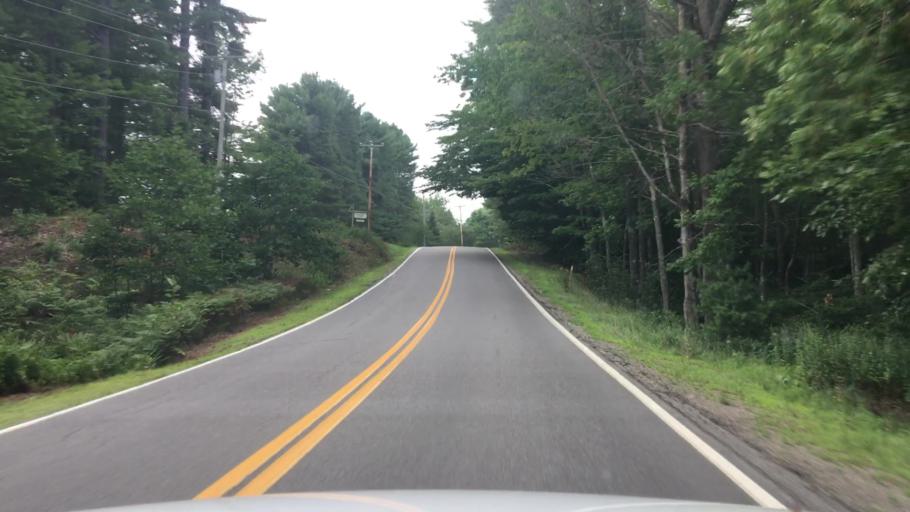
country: US
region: Maine
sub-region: Knox County
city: Washington
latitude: 44.2944
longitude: -69.3622
